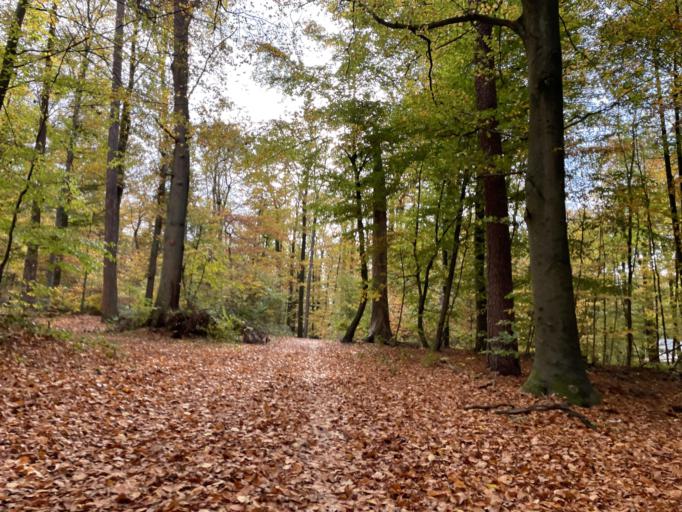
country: DE
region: Lower Saxony
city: Melbeck
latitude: 53.2165
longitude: 10.3974
